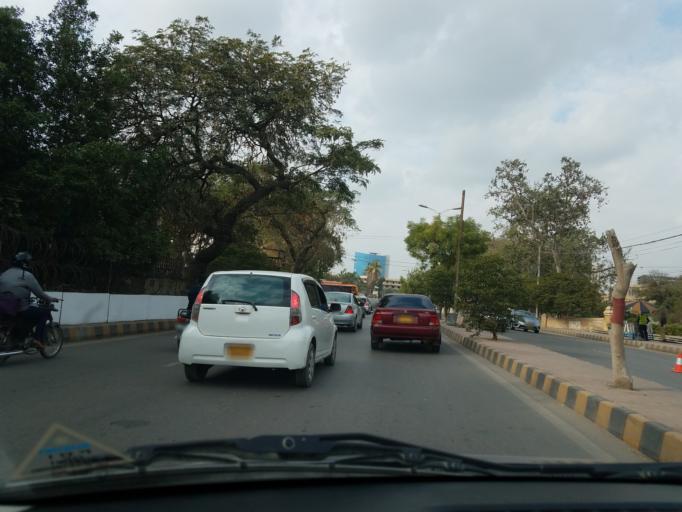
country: PK
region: Sindh
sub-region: Karachi District
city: Karachi
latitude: 24.8466
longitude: 67.0315
